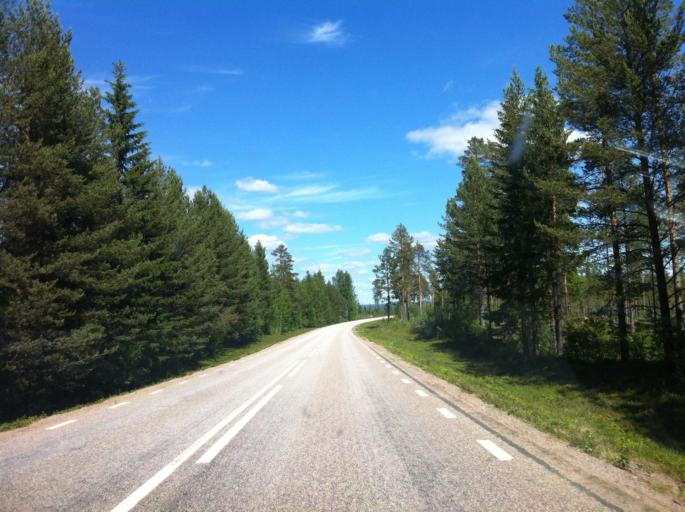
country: SE
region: Gaevleborg
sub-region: Ljusdals Kommun
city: Farila
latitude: 61.9895
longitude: 15.1468
